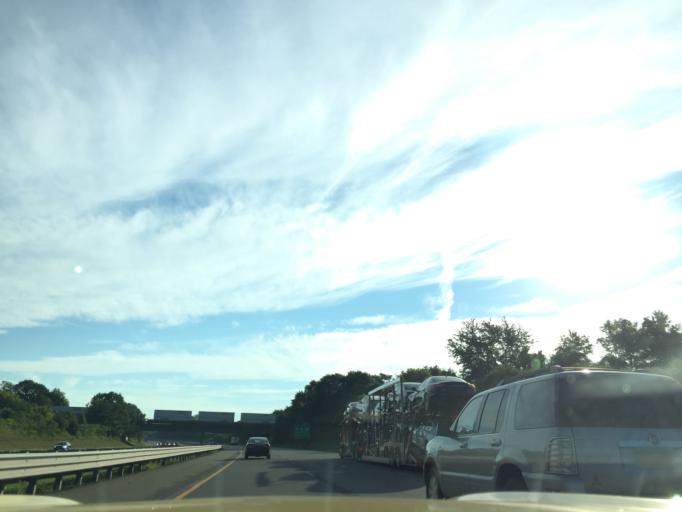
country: US
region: New Jersey
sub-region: Warren County
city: Alpha
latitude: 40.6536
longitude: -75.1500
